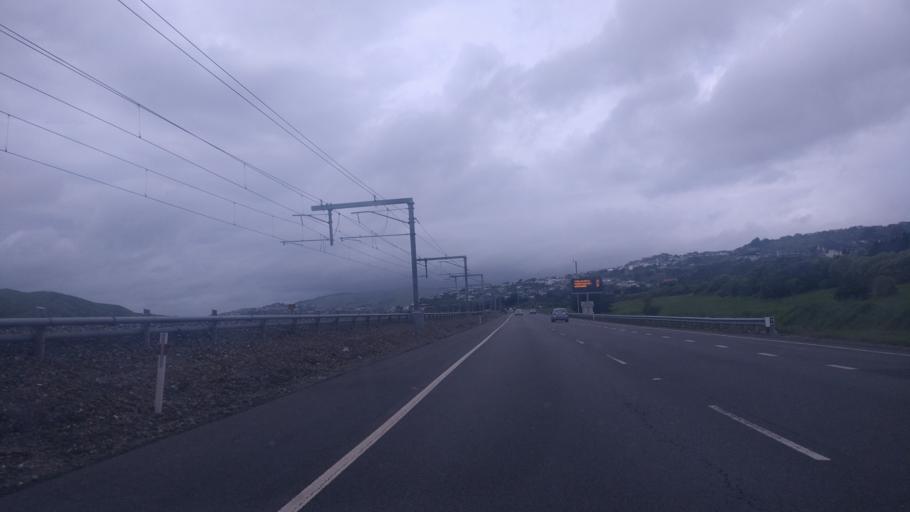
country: NZ
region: Wellington
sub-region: Porirua City
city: Porirua
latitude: -41.1190
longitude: 174.8552
